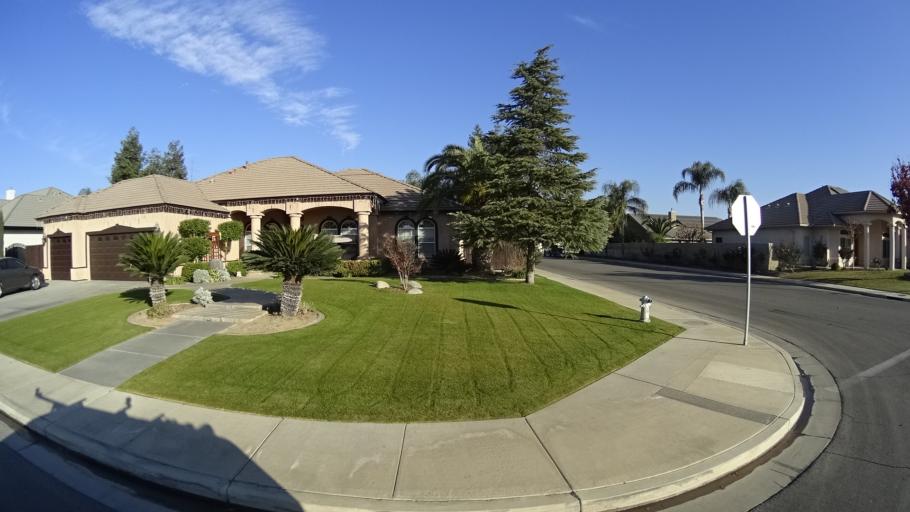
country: US
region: California
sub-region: Kern County
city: Greenfield
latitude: 35.2766
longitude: -119.0539
